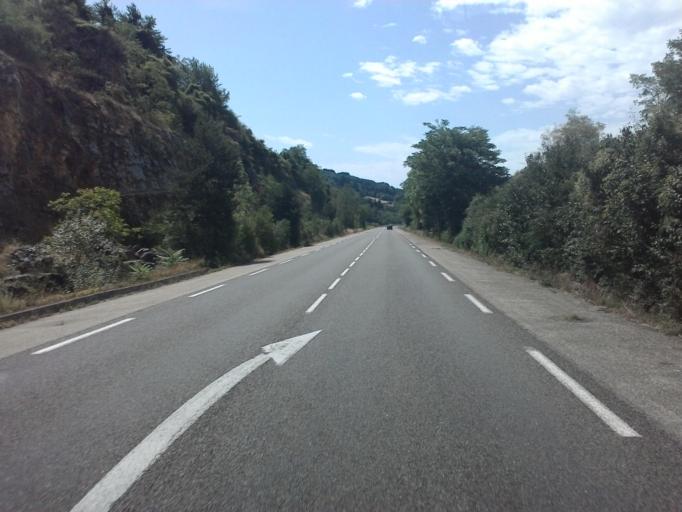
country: FR
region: Franche-Comte
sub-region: Departement du Jura
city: Cousance
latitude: 46.5326
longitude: 5.3964
